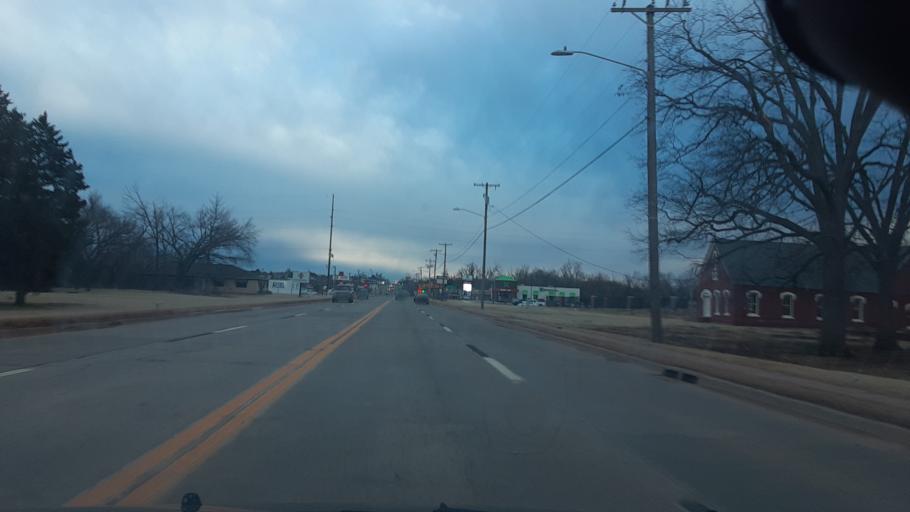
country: US
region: Oklahoma
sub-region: Logan County
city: Guthrie
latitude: 35.8683
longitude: -97.4254
